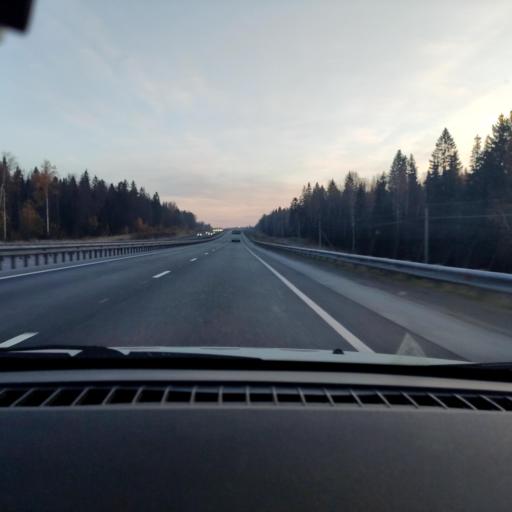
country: RU
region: Perm
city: Ferma
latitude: 58.0203
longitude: 56.4172
